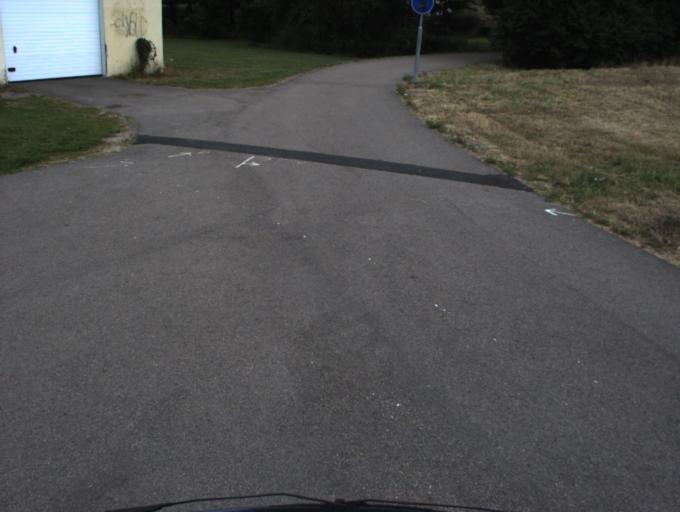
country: SE
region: Skane
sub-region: Helsingborg
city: Rydeback
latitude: 55.9679
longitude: 12.7771
